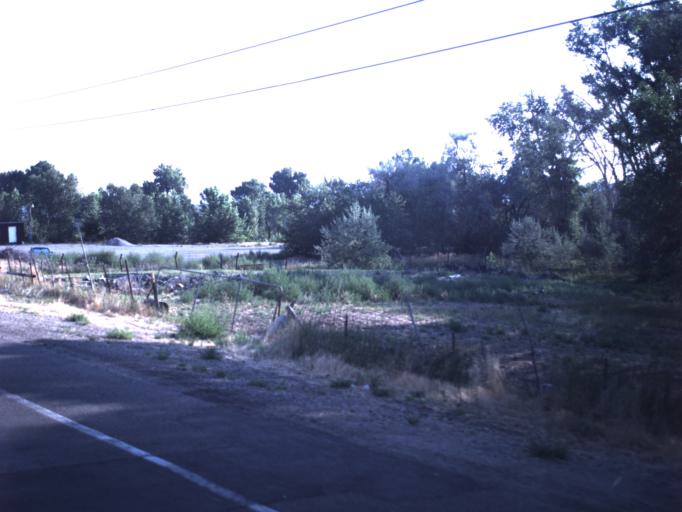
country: US
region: Utah
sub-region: Uintah County
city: Vernal
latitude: 40.4712
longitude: -109.5288
